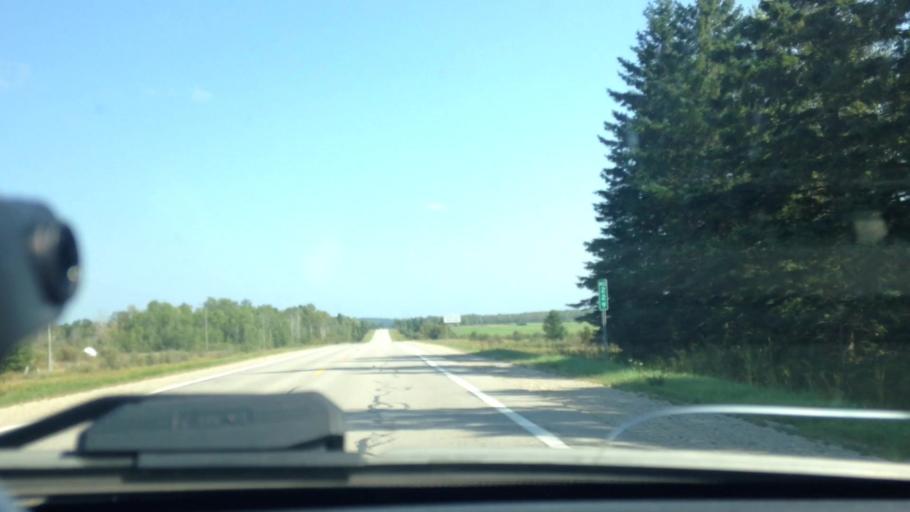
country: US
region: Michigan
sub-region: Luce County
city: Newberry
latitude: 46.3102
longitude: -85.6130
